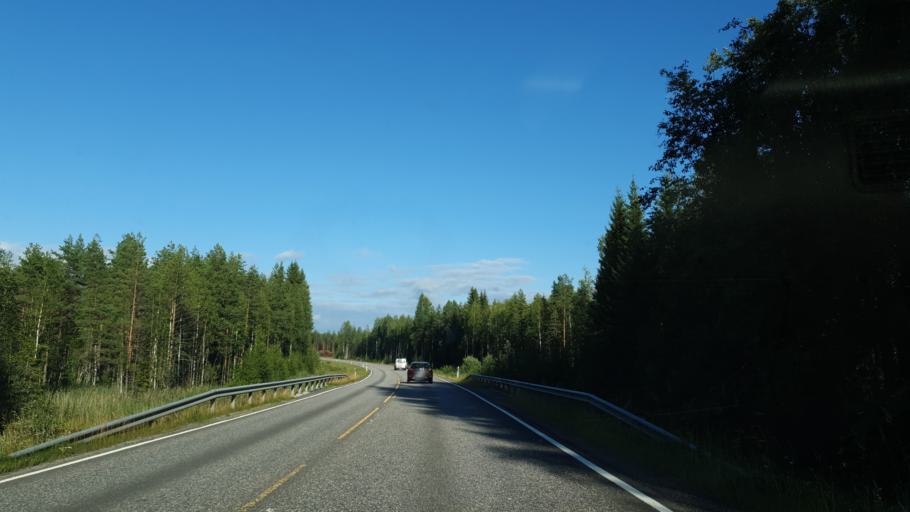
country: FI
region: North Karelia
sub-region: Joensuu
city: Outokumpu
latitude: 62.5200
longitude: 29.0125
